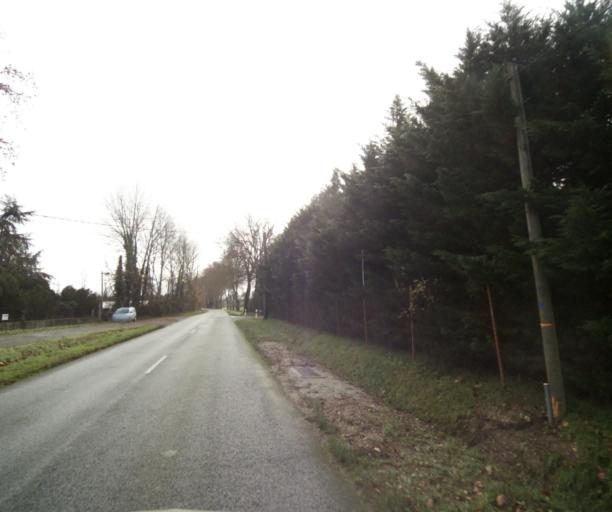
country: FR
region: Midi-Pyrenees
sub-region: Departement de la Haute-Garonne
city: Villemur-sur-Tarn
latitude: 43.8782
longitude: 1.4860
